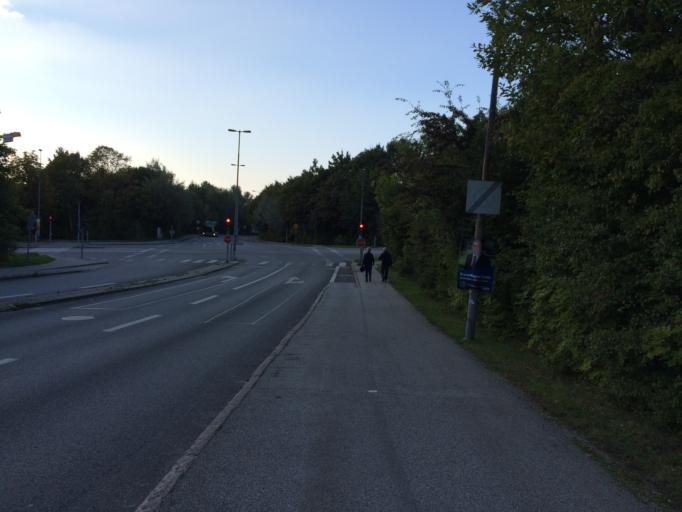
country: SE
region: Skane
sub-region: Lunds Kommun
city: Lund
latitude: 55.6994
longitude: 13.2331
